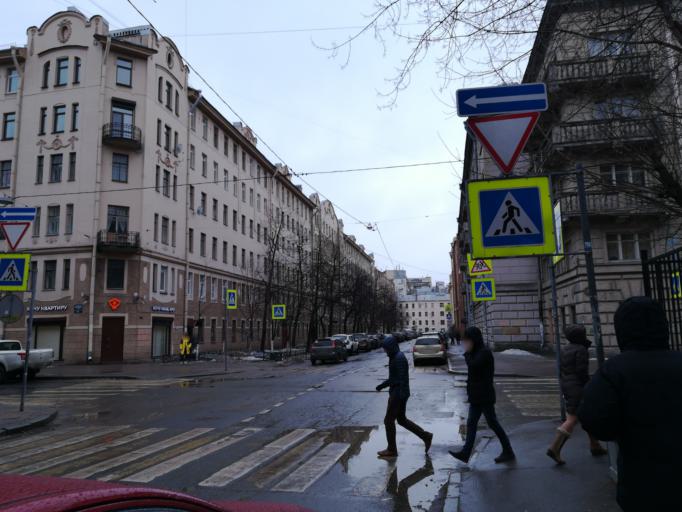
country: RU
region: St.-Petersburg
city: Petrogradka
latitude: 59.9596
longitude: 30.3262
